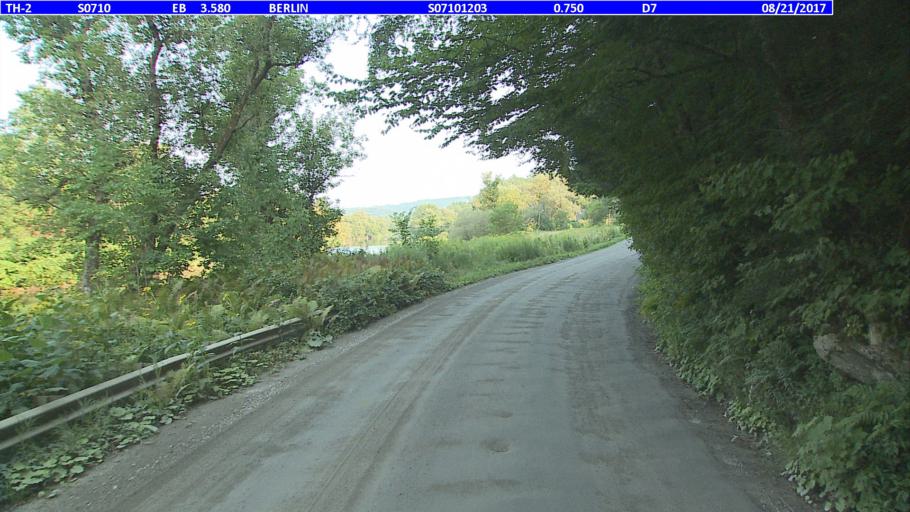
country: US
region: Vermont
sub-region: Washington County
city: Montpelier
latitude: 44.2642
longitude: -72.6275
